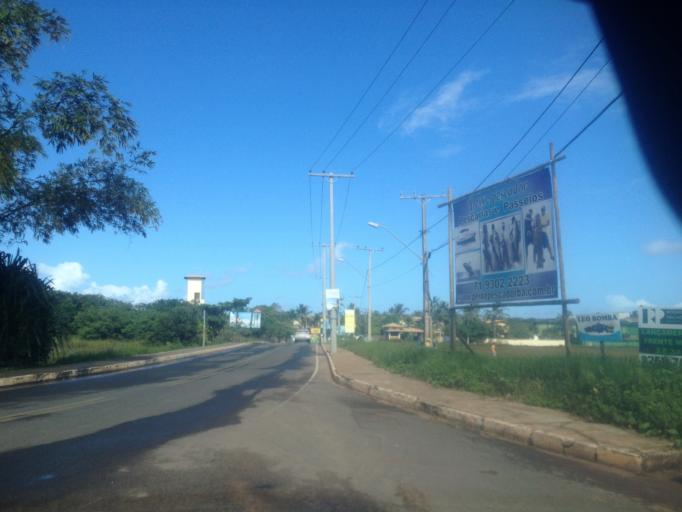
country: BR
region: Bahia
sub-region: Mata De Sao Joao
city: Mata de Sao Joao
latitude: -12.6049
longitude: -38.0410
